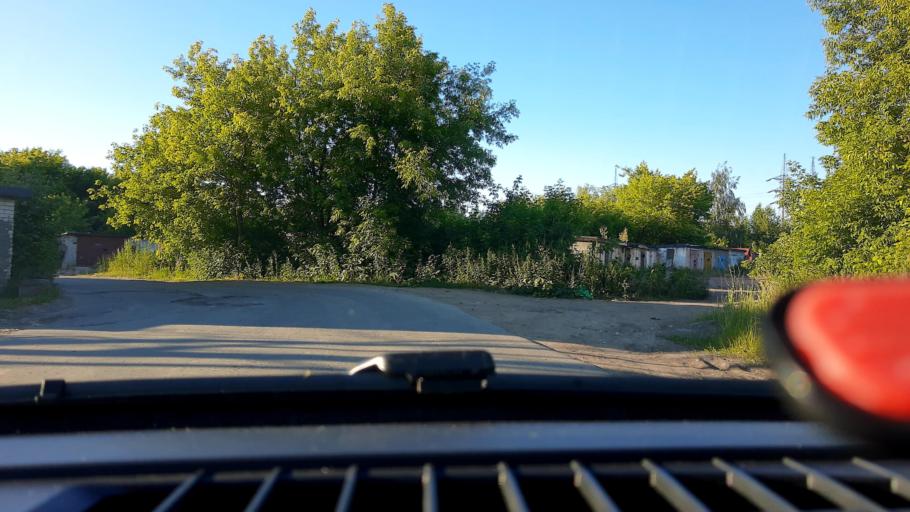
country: RU
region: Nizjnij Novgorod
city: Nizhniy Novgorod
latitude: 56.3009
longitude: 43.8855
